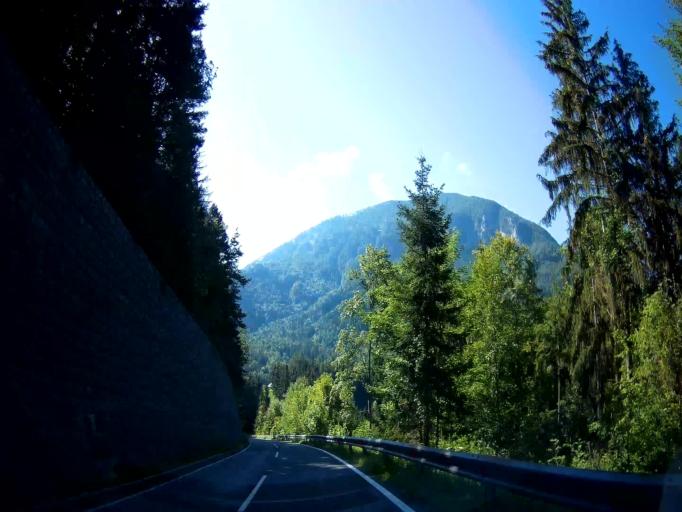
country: AT
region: Carinthia
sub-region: Politischer Bezirk Volkermarkt
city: Gallizien
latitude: 46.5440
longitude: 14.4721
